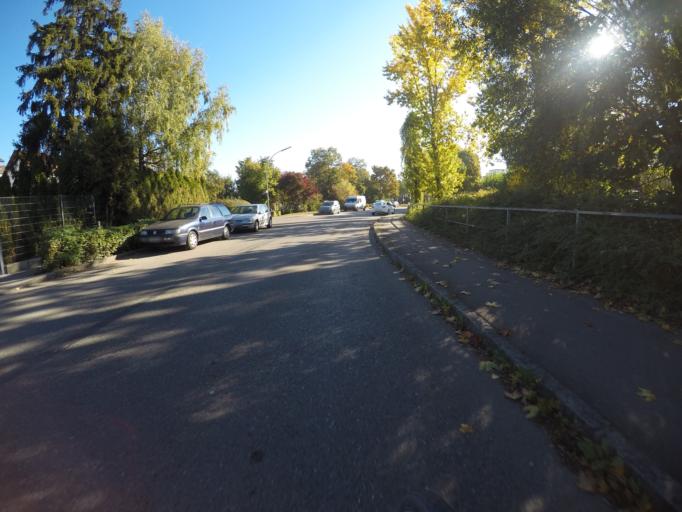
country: DE
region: Baden-Wuerttemberg
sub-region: Regierungsbezirk Stuttgart
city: Filderstadt
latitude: 48.6738
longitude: 9.2133
